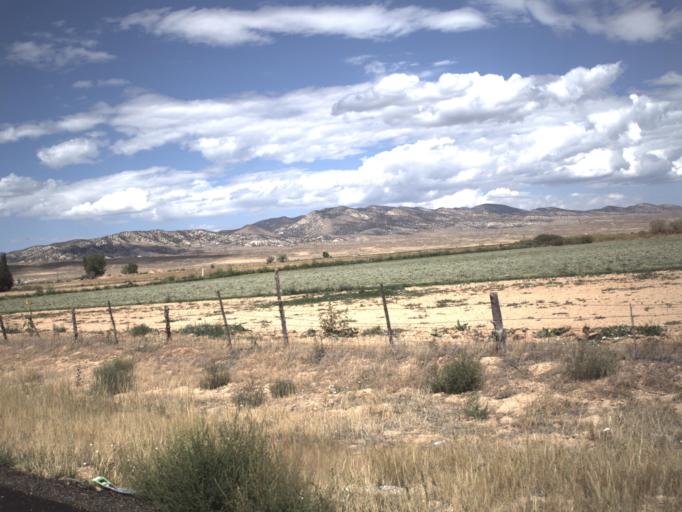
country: US
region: Utah
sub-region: Sevier County
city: Aurora
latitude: 38.9552
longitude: -111.9125
